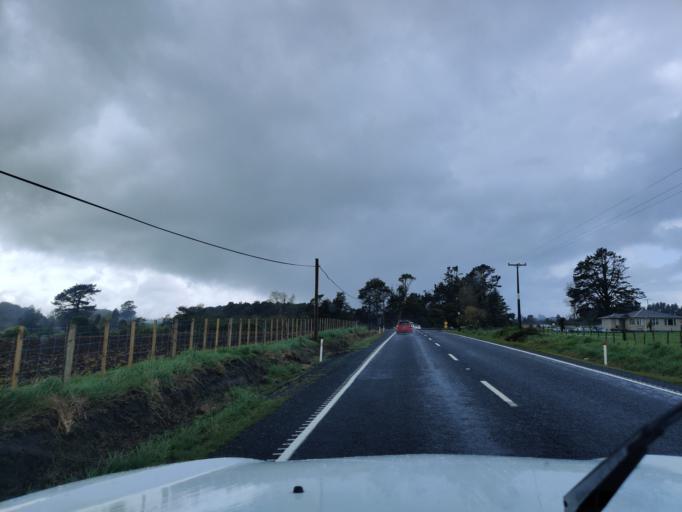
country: NZ
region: Waikato
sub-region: Matamata-Piako District
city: Matamata
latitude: -37.9970
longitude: 175.8634
